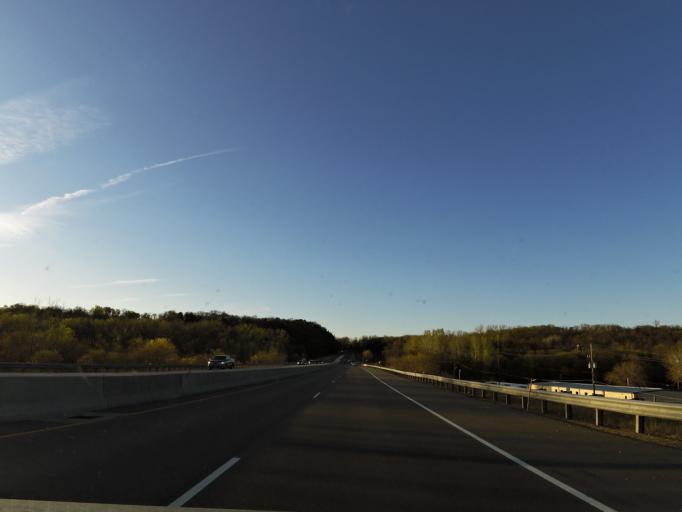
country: US
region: Minnesota
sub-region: Dakota County
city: Hastings
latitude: 44.7543
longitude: -92.8531
